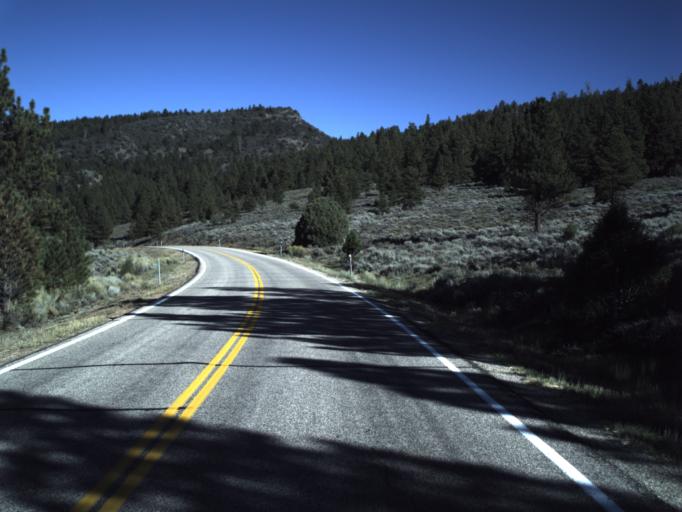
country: US
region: Utah
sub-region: Garfield County
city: Panguitch
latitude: 37.7222
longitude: -112.6200
